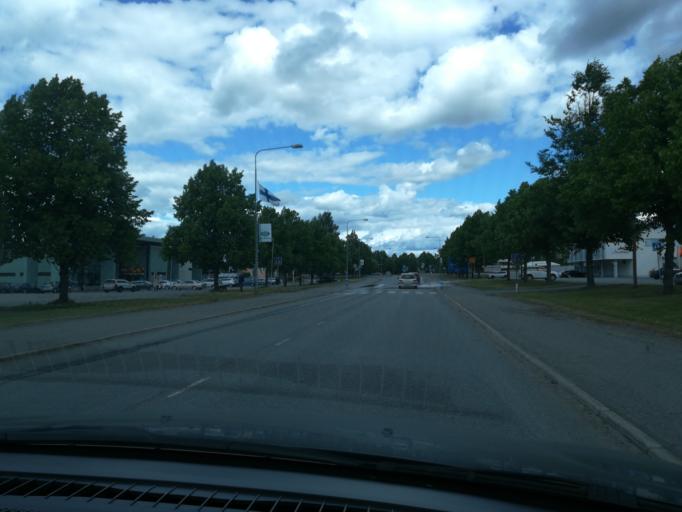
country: FI
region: Southern Savonia
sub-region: Mikkeli
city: Maentyharju
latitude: 61.4157
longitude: 26.8805
